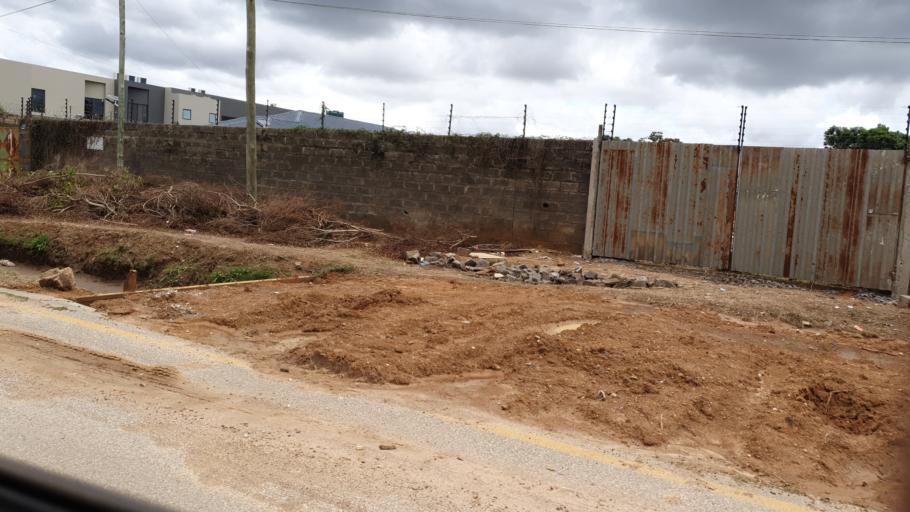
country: ZM
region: Lusaka
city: Lusaka
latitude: -15.4222
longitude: 28.2993
